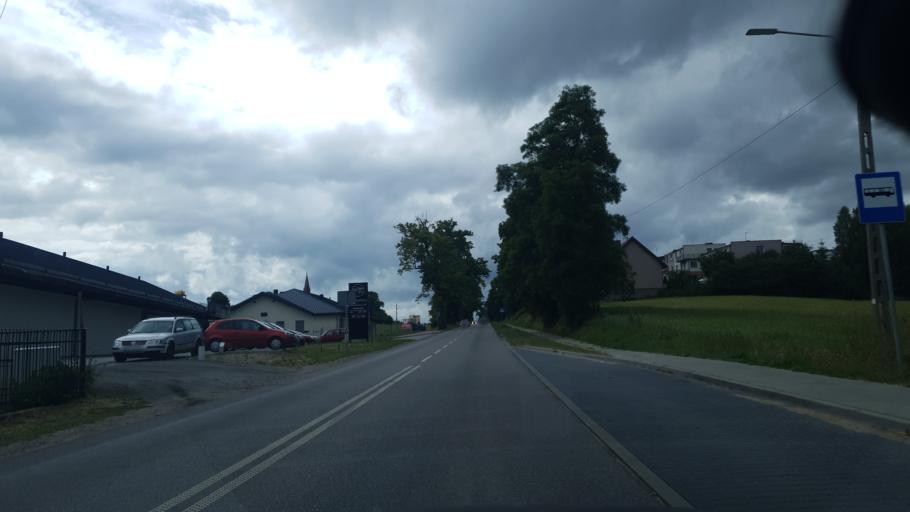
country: PL
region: Pomeranian Voivodeship
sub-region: Powiat kartuski
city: Przodkowo
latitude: 54.3778
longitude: 18.2963
